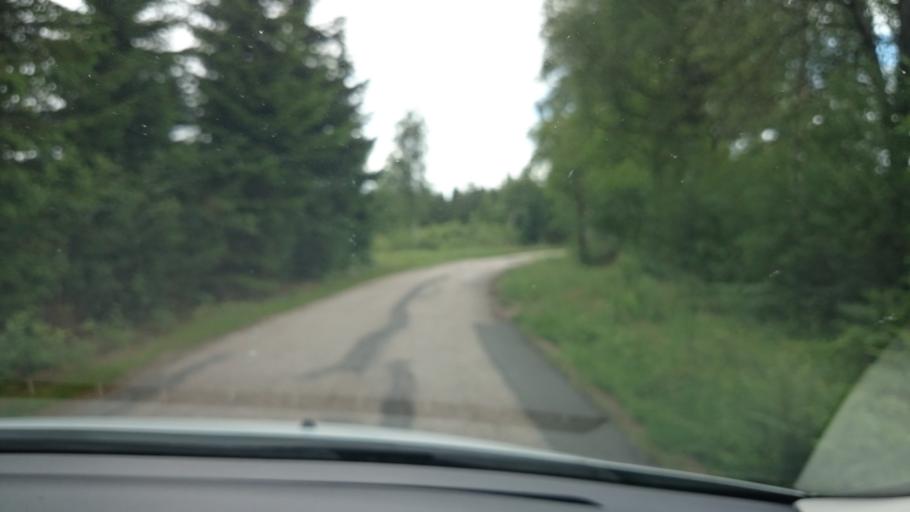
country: SE
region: Halland
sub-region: Hylte Kommun
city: Hyltebruk
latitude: 56.9703
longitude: 13.1969
